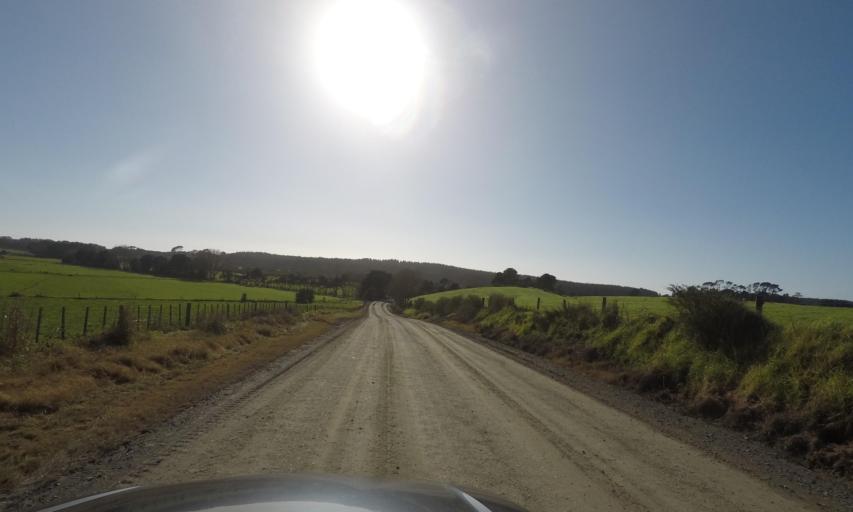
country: NZ
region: Auckland
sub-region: Auckland
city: Wellsford
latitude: -36.1591
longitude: 174.6119
